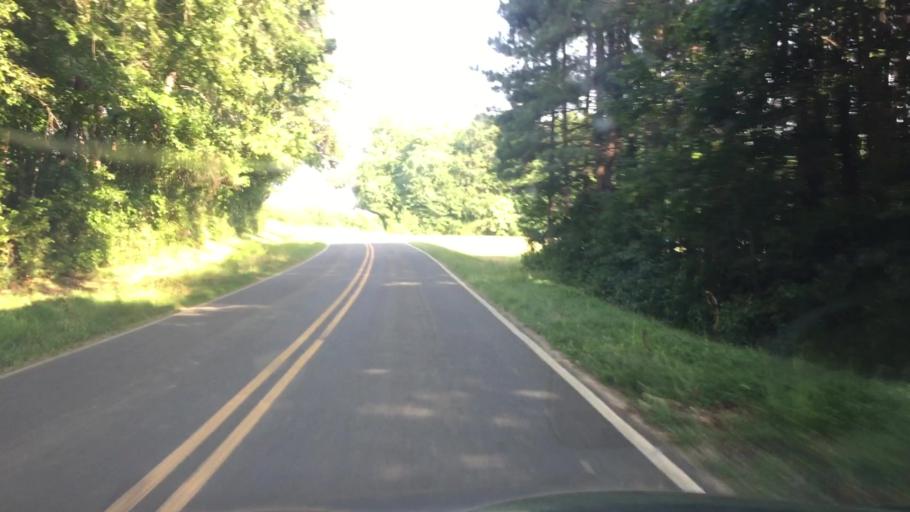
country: US
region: North Carolina
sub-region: Rockingham County
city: Reidsville
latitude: 36.2780
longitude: -79.5901
